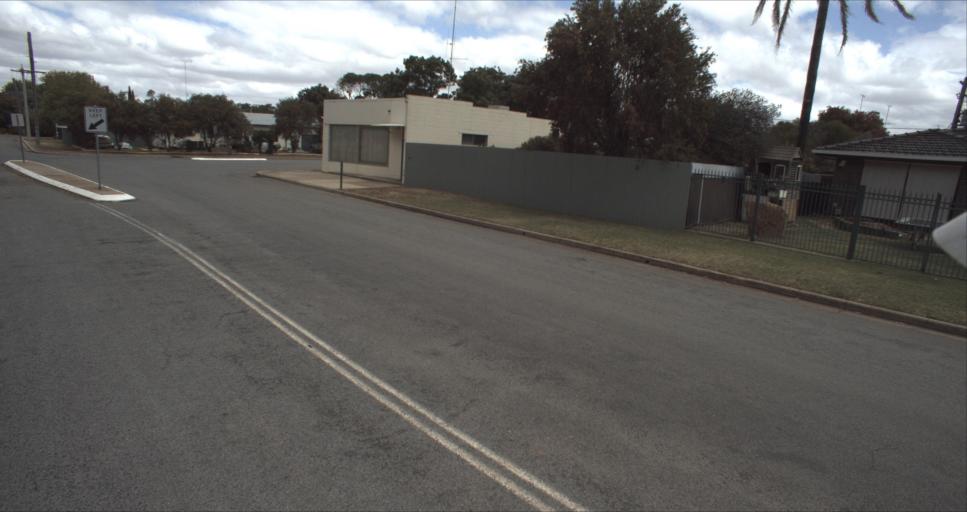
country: AU
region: New South Wales
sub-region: Leeton
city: Leeton
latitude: -34.5542
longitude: 146.3913
